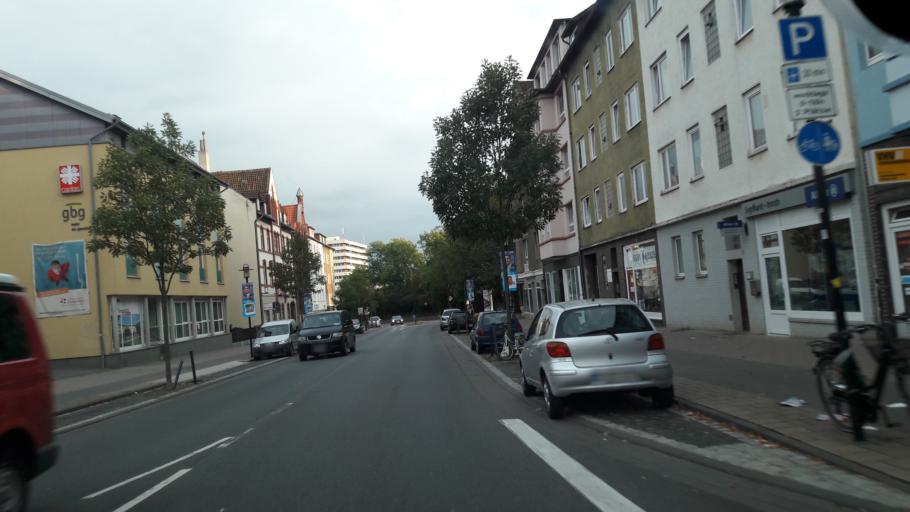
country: DE
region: Lower Saxony
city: Hildesheim
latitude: 52.1607
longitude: 9.9483
